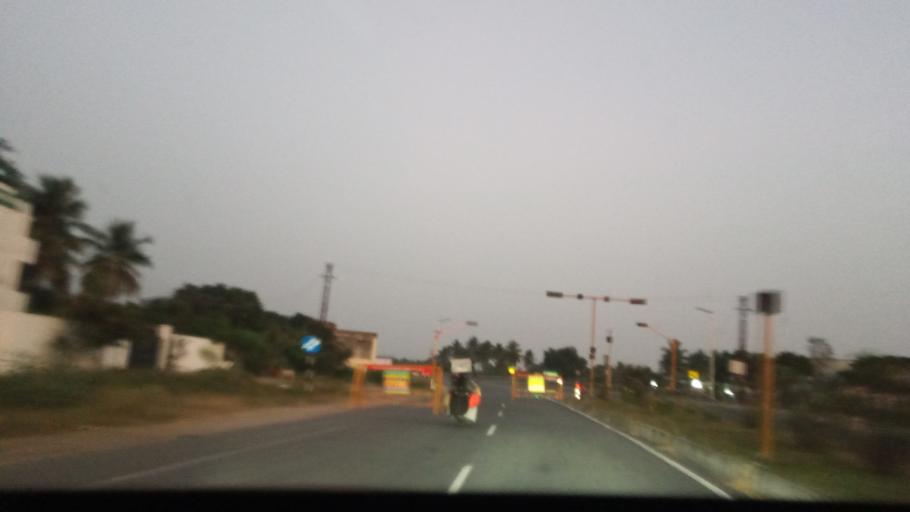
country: IN
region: Tamil Nadu
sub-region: Salem
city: Attur
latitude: 11.6146
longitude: 78.5637
